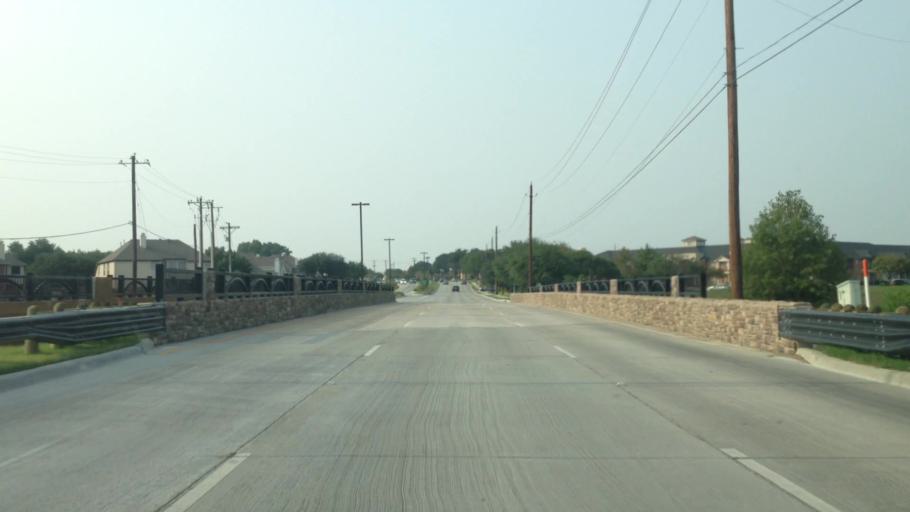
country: US
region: Texas
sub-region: Dallas County
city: Carrollton
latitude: 33.0059
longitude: -96.9099
